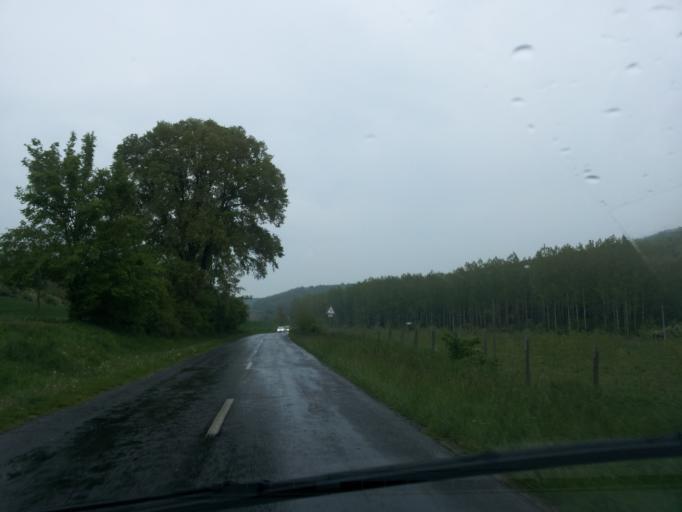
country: HU
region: Tolna
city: Szekszard
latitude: 46.2836
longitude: 18.6488
